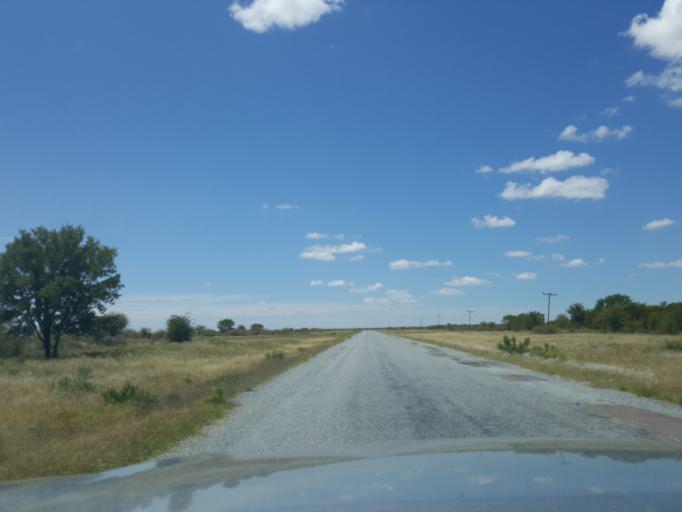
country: BW
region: Central
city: Gweta
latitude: -20.1380
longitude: 25.6661
